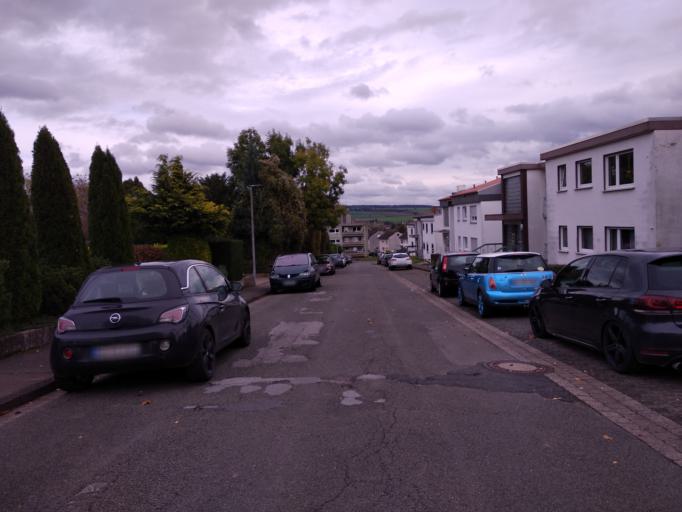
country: DE
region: North Rhine-Westphalia
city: Beverungen
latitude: 51.6634
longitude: 9.3612
